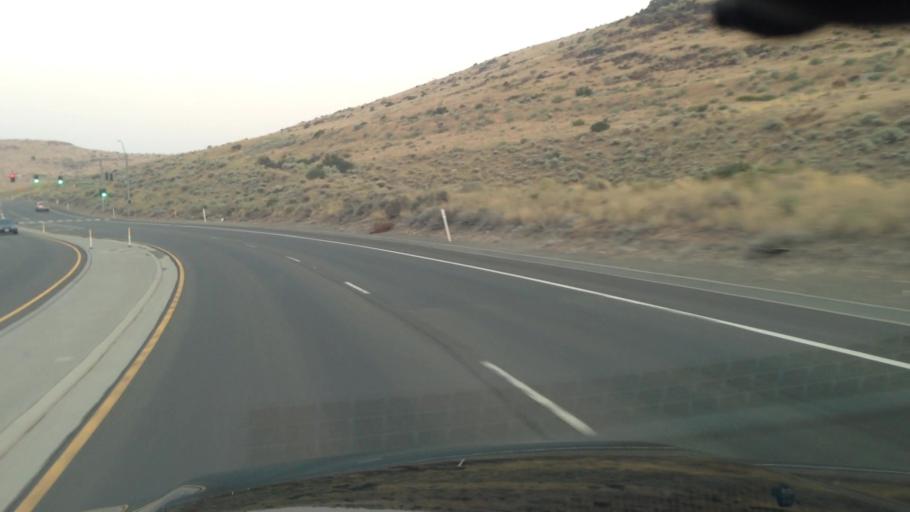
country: US
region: Nevada
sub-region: Washoe County
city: Reno
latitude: 39.4784
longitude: -119.8457
